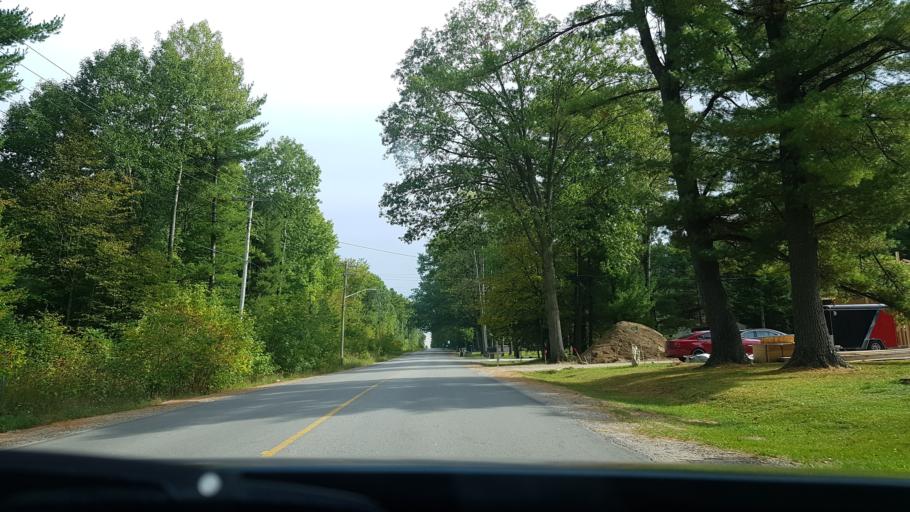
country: CA
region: Ontario
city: Barrie
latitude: 44.4860
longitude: -79.8176
